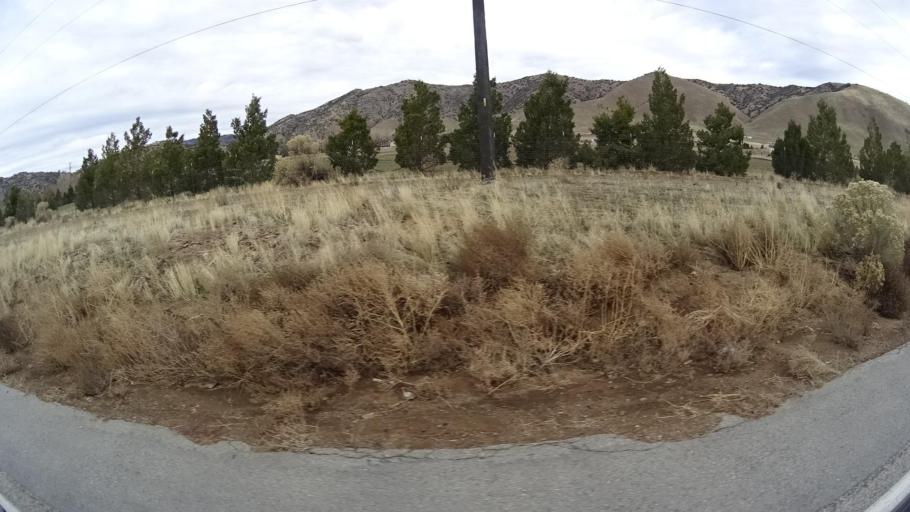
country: US
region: California
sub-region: Kern County
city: Bear Valley Springs
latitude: 35.1307
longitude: -118.5728
